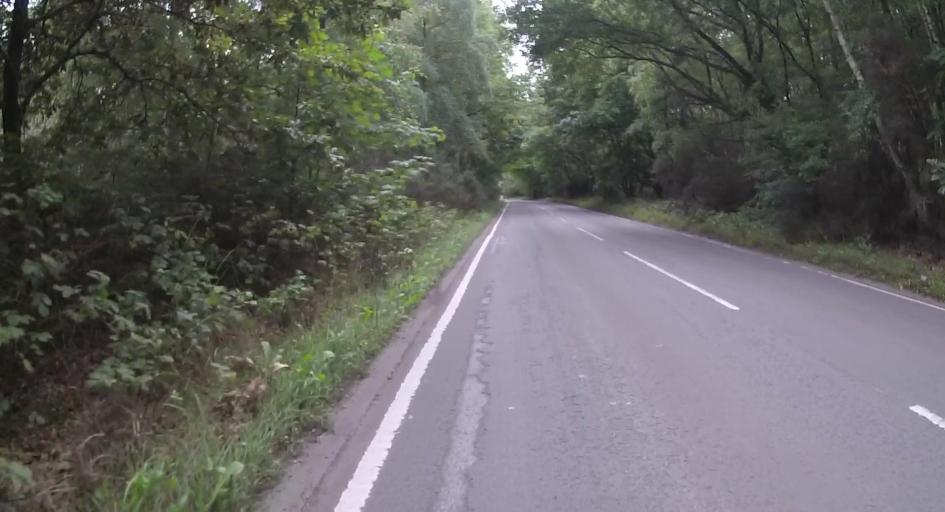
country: GB
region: England
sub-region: Surrey
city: Pirbright
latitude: 51.3110
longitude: -0.6487
